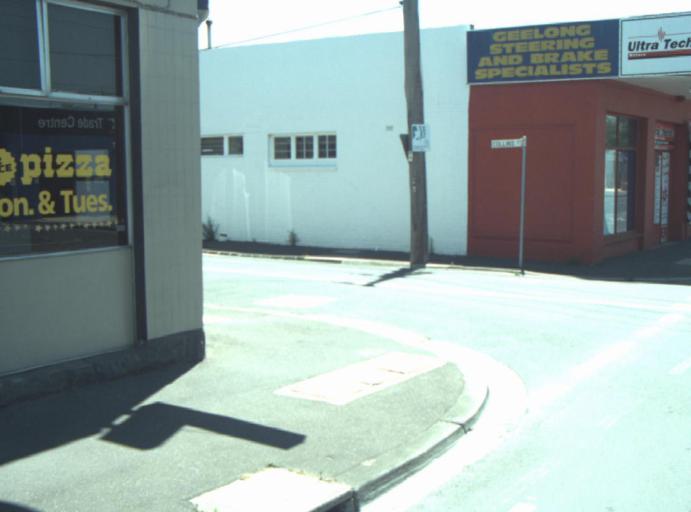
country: AU
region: Victoria
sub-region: Greater Geelong
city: Geelong West
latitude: -38.1369
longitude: 144.3490
